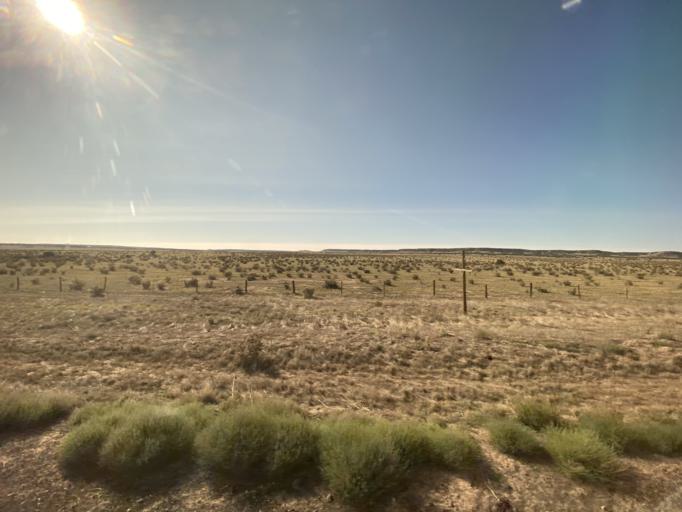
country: US
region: Colorado
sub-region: Otero County
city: Fowler
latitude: 37.5673
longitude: -104.0715
